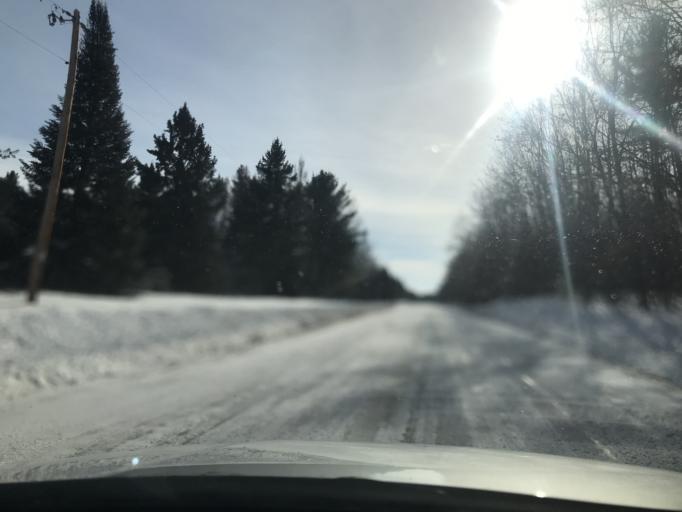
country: US
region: Wisconsin
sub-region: Oconto County
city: Gillett
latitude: 45.1276
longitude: -88.2498
